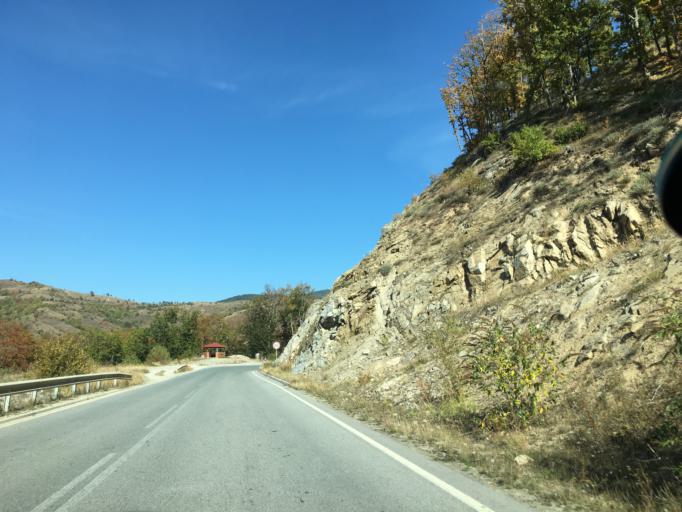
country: BG
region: Smolyan
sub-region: Obshtina Devin
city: Devin
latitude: 41.7838
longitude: 24.4615
